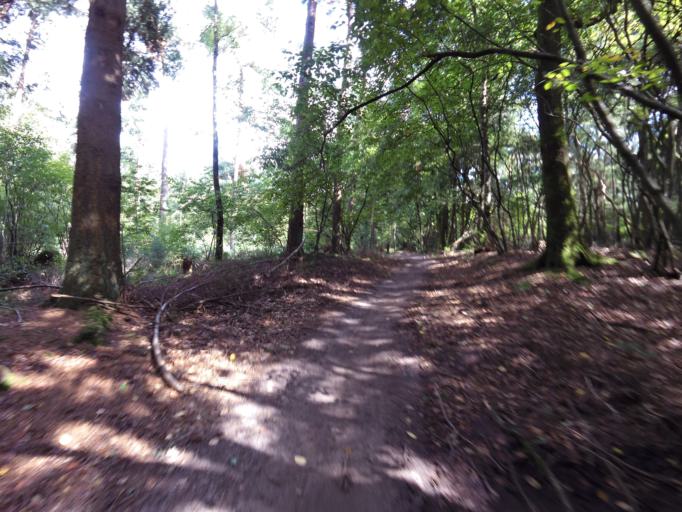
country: NL
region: North Brabant
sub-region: Gemeente Loon op Zand
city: Loon op Zand
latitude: 51.6374
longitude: 5.0884
